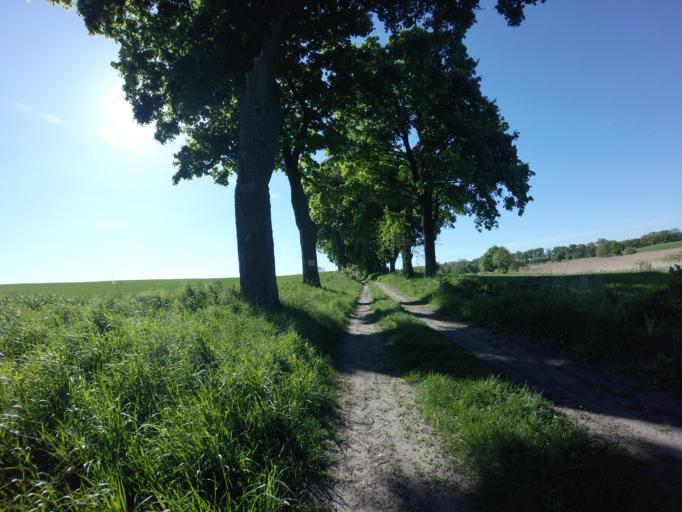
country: PL
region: West Pomeranian Voivodeship
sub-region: Powiat stargardzki
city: Dolice
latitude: 53.1576
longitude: 15.2958
